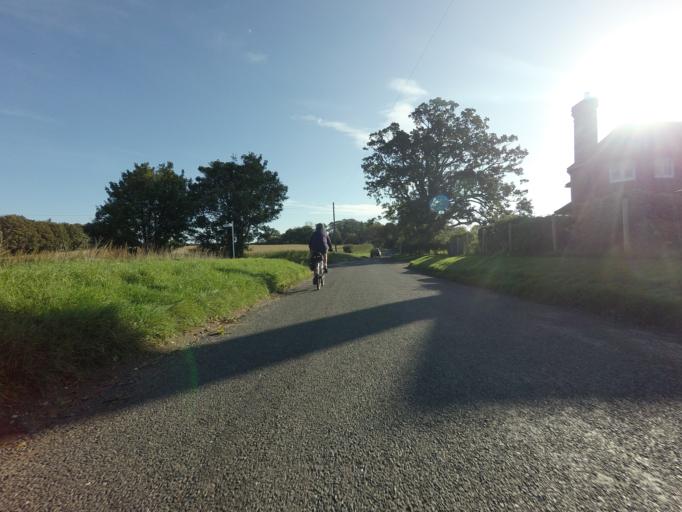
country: GB
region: England
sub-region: Norfolk
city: Dersingham
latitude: 52.8364
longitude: 0.5773
